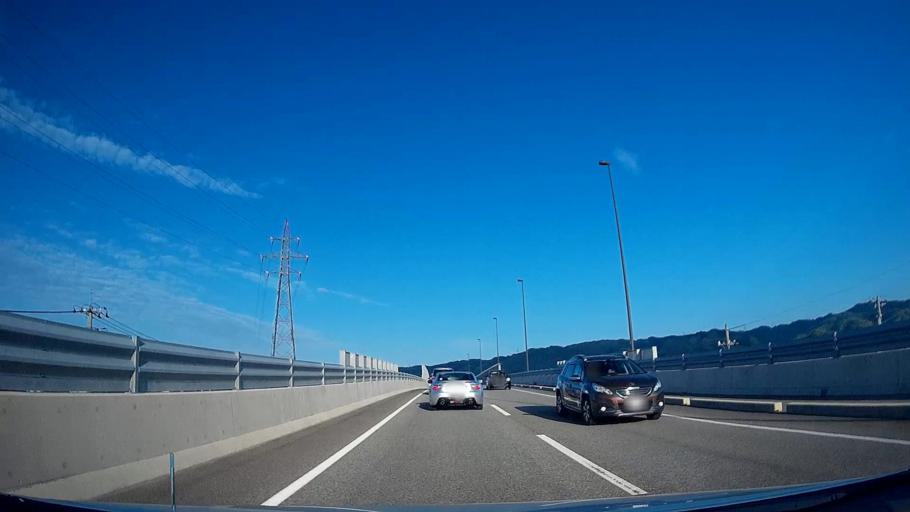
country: JP
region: Ishikawa
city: Nanao
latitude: 37.0333
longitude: 136.9588
